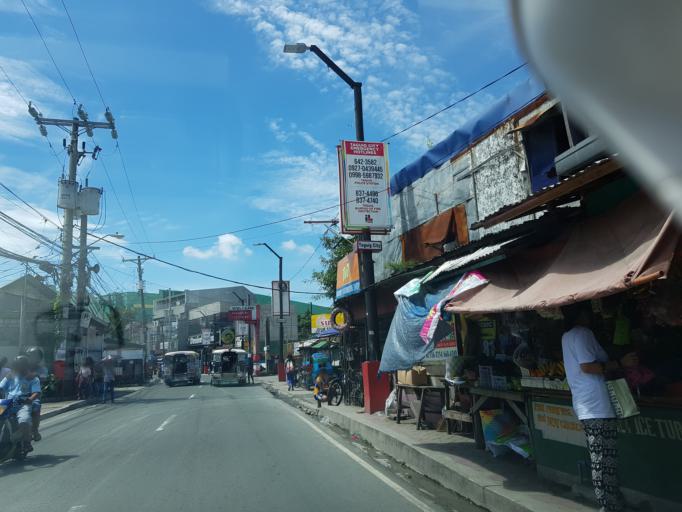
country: PH
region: Calabarzon
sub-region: Province of Rizal
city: Pateros
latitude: 14.5314
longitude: 121.0695
